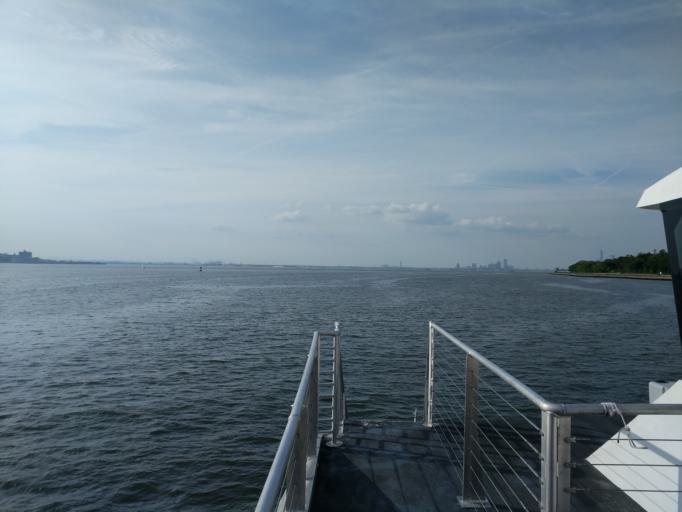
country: US
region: New York
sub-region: Kings County
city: Bensonhurst
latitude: 40.6180
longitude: -74.0440
